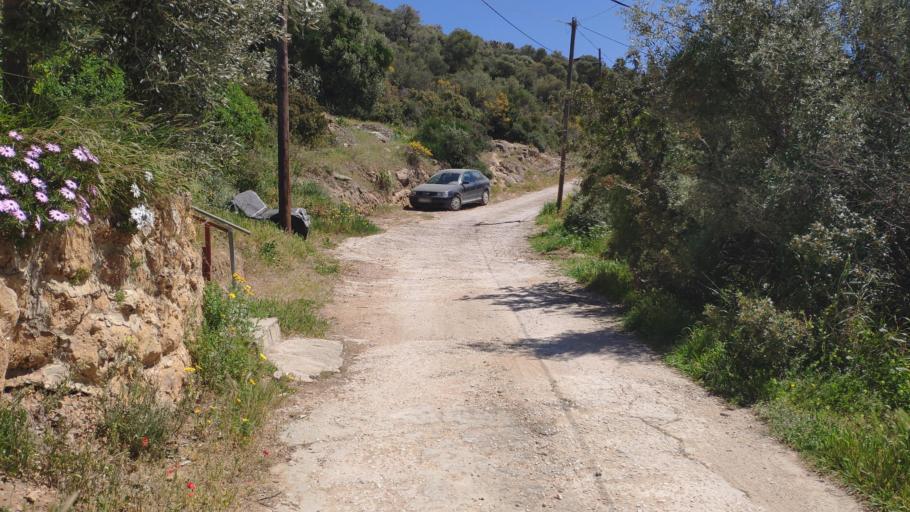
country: GR
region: Attica
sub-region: Nomarchia Anatolikis Attikis
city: Limin Mesoyaias
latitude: 37.9006
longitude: 24.0329
